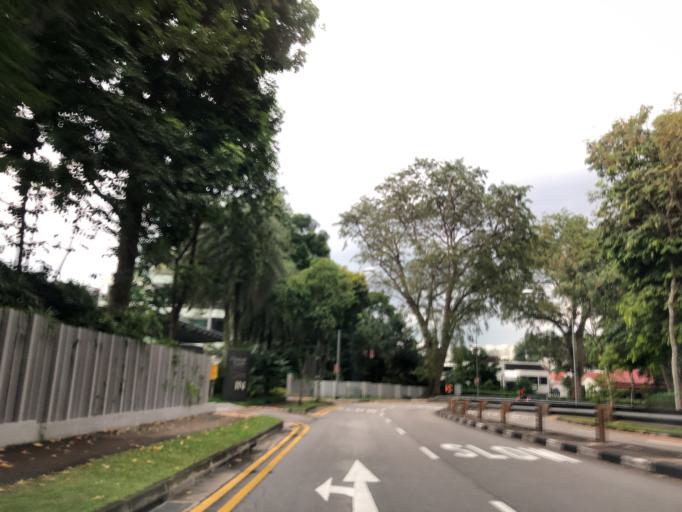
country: SG
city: Singapore
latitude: 1.3131
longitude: 103.8254
